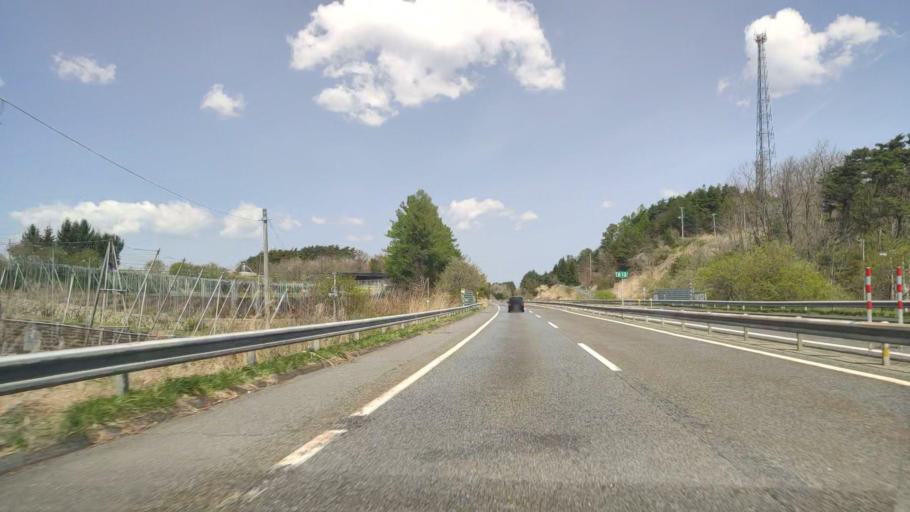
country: JP
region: Aomori
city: Hachinohe
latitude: 40.3397
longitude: 141.4510
